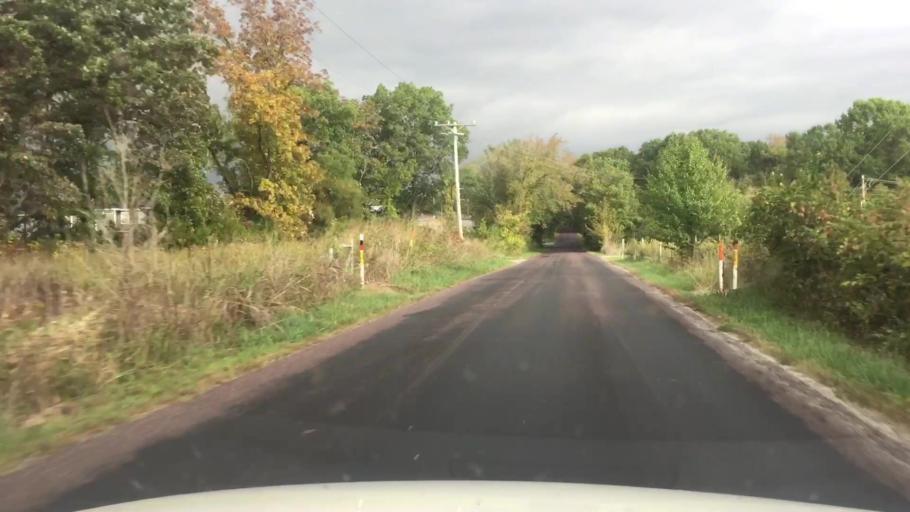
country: US
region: Missouri
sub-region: Boone County
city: Columbia
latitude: 38.8684
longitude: -92.3738
